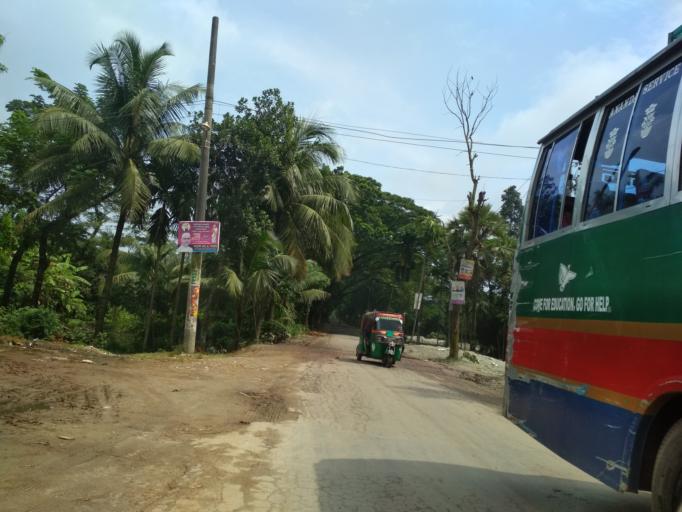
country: BD
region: Chittagong
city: Lakshmipur
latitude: 22.9493
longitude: 90.8086
